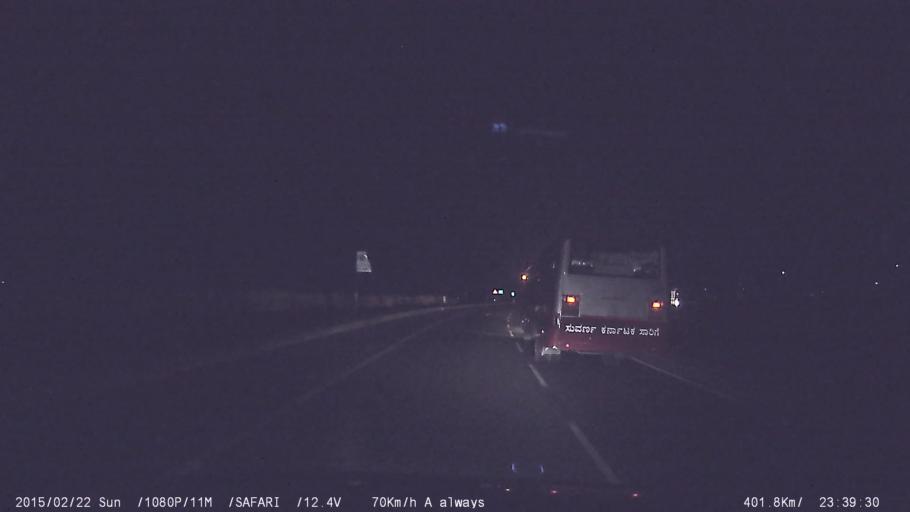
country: IN
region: Tamil Nadu
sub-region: Salem
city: Omalur
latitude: 11.7168
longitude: 78.0765
